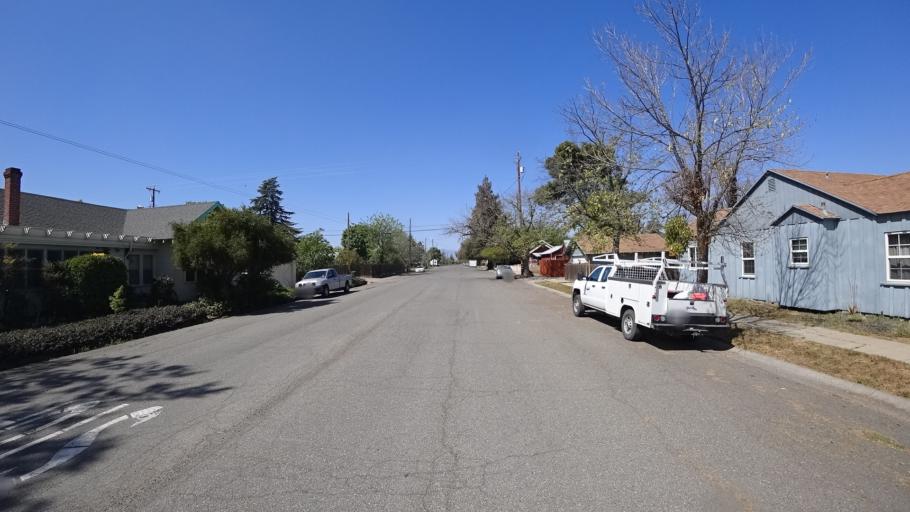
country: US
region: California
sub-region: Glenn County
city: Willows
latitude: 39.5154
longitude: -122.1984
